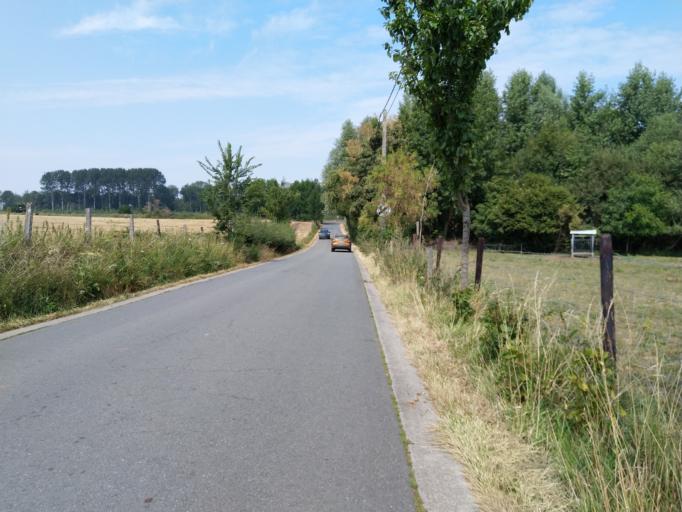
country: BE
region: Wallonia
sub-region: Province du Hainaut
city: Soignies
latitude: 50.5338
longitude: 4.0270
